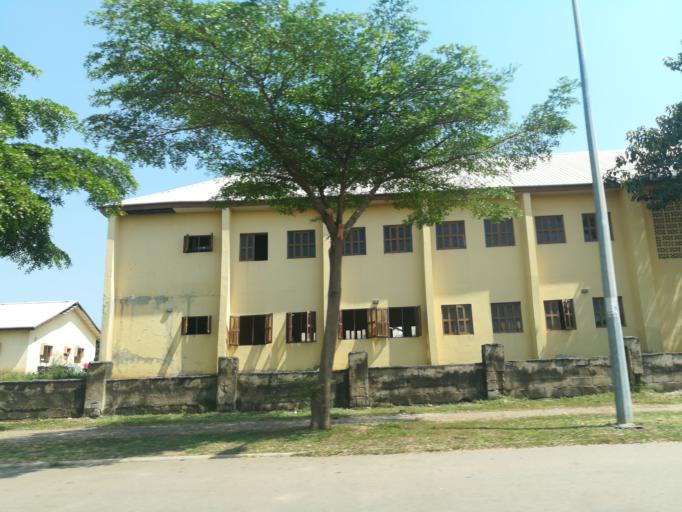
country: NG
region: Abuja Federal Capital Territory
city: Abuja
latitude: 9.0677
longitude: 7.4272
